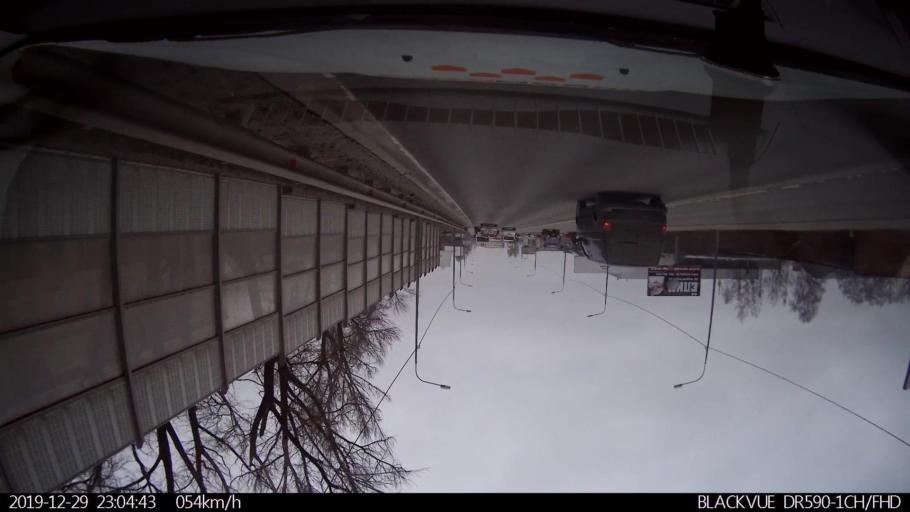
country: RU
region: Nizjnij Novgorod
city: Afonino
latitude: 56.2680
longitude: 44.0923
